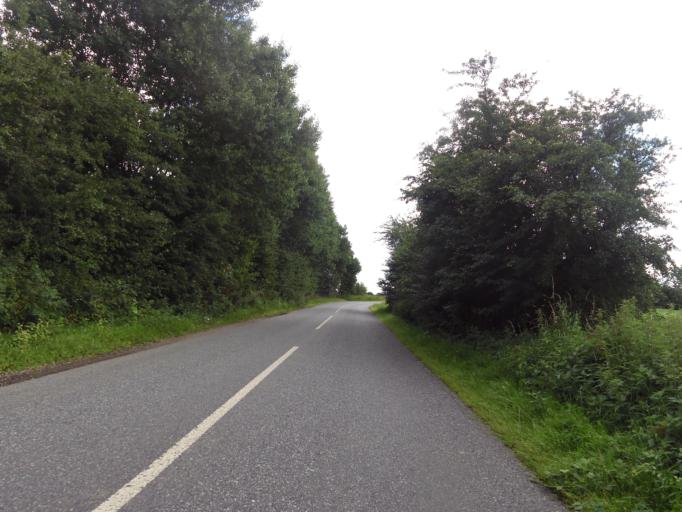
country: DK
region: South Denmark
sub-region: Haderslev Kommune
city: Vojens
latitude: 55.2816
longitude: 9.2565
